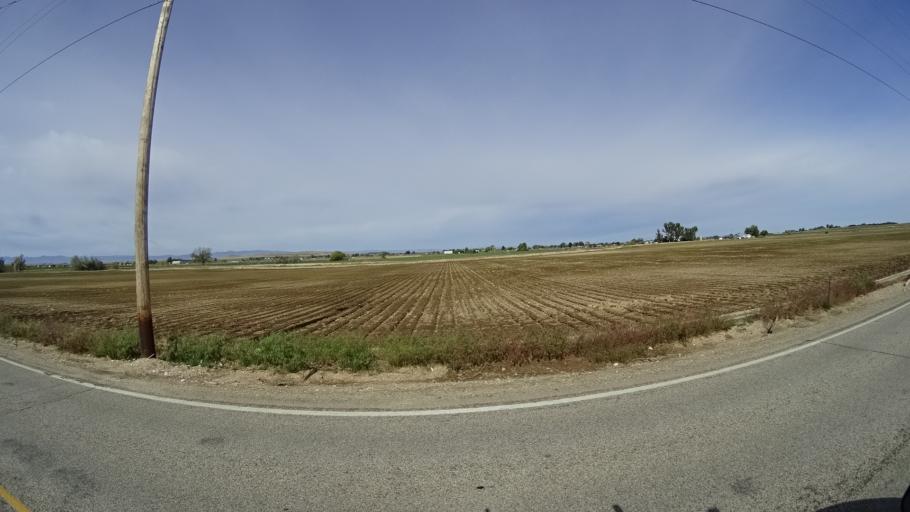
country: US
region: Idaho
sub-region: Ada County
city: Kuna
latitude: 43.4704
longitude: -116.3341
